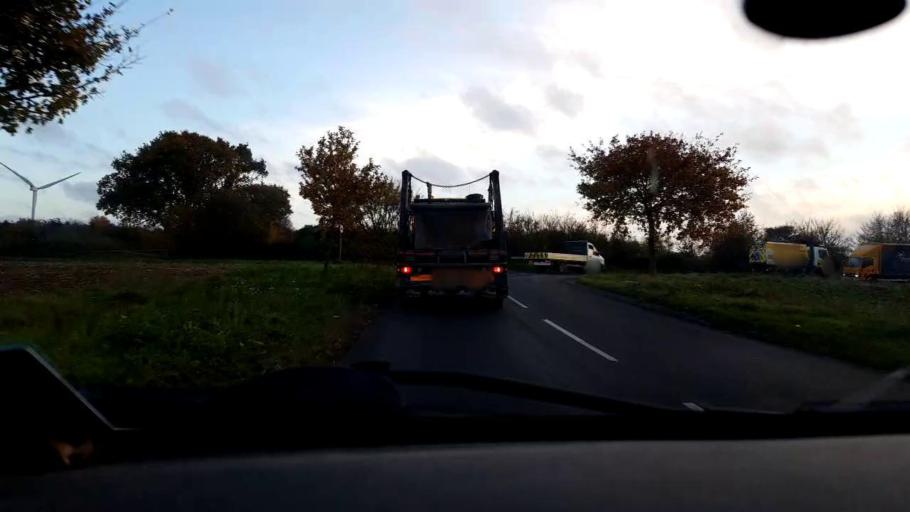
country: GB
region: England
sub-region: Norfolk
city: Mattishall
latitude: 52.6977
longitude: 1.0998
